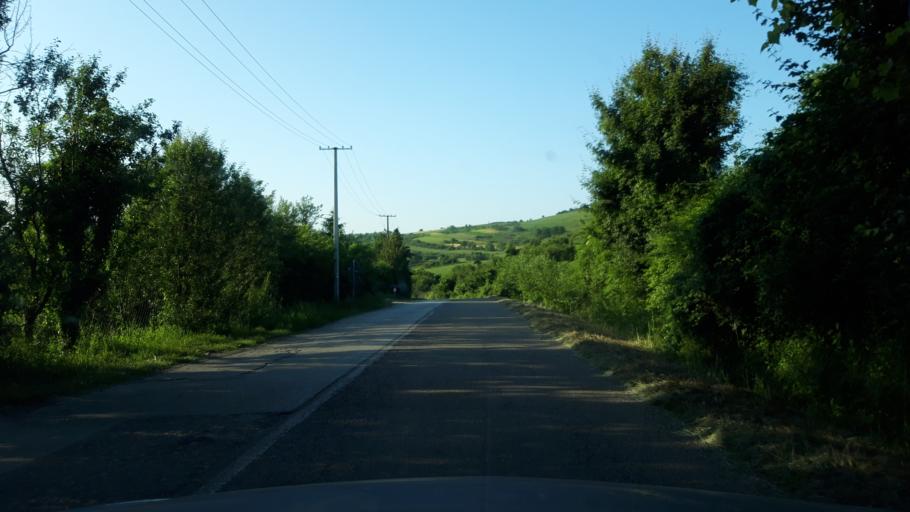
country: RS
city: Glozan
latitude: 45.1652
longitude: 19.5881
